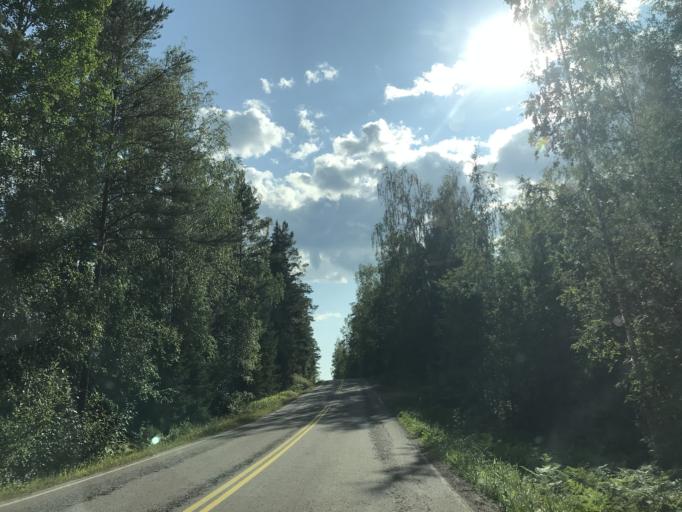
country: FI
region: Uusimaa
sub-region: Helsinki
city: Vihti
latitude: 60.4434
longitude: 24.5616
